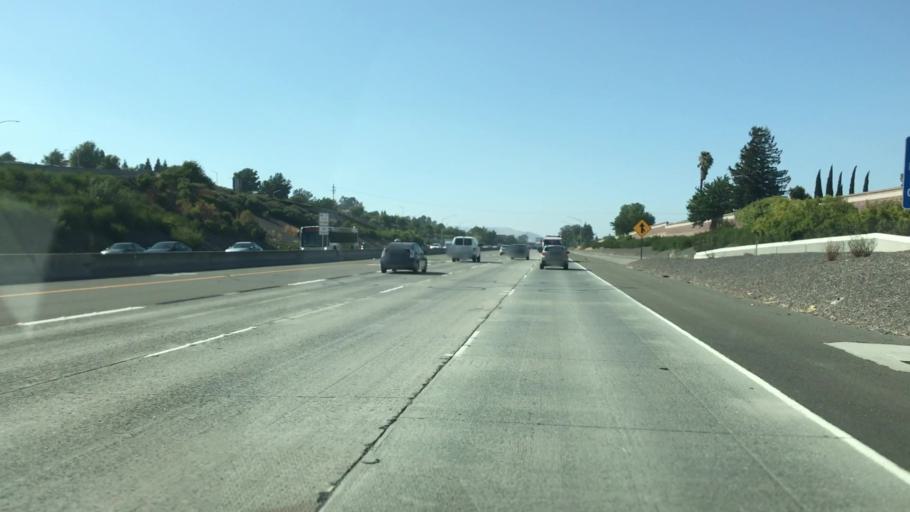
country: US
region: California
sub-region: Alameda County
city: Dublin
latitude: 37.7246
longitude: -121.9408
